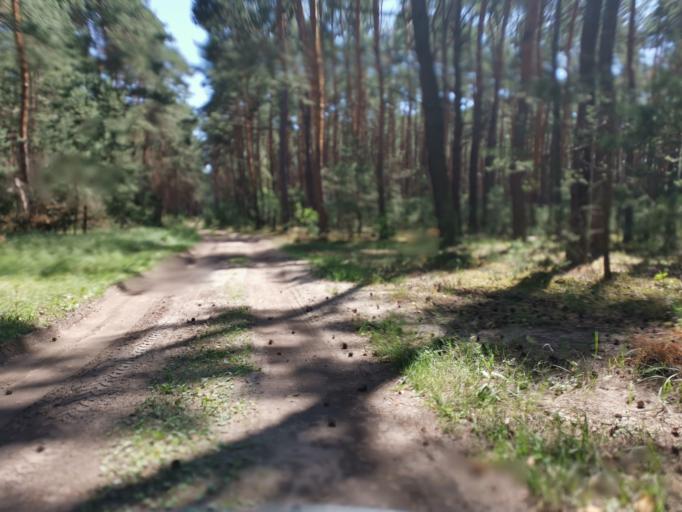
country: CZ
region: South Moravian
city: Vracov
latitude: 48.9621
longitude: 17.2216
